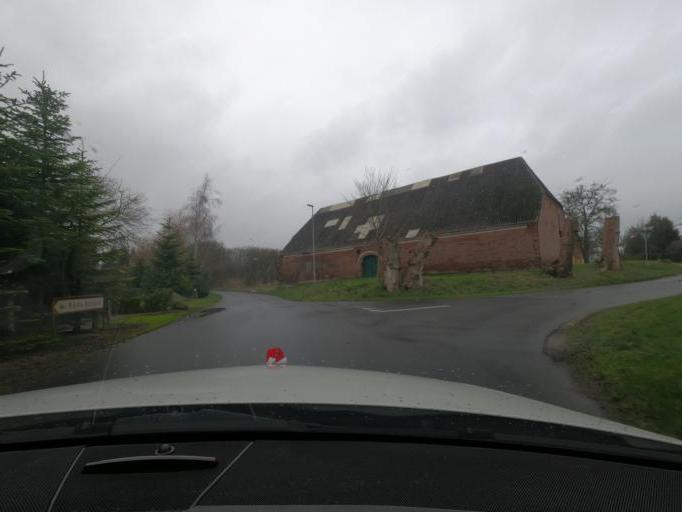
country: DK
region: South Denmark
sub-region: Haderslev Kommune
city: Starup
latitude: 55.2463
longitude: 9.6847
